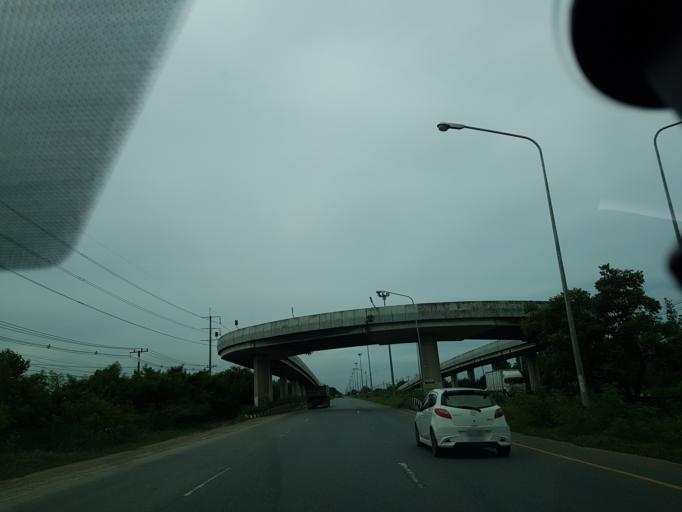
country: TH
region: Pathum Thani
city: Sam Khok
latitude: 14.1040
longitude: 100.5703
